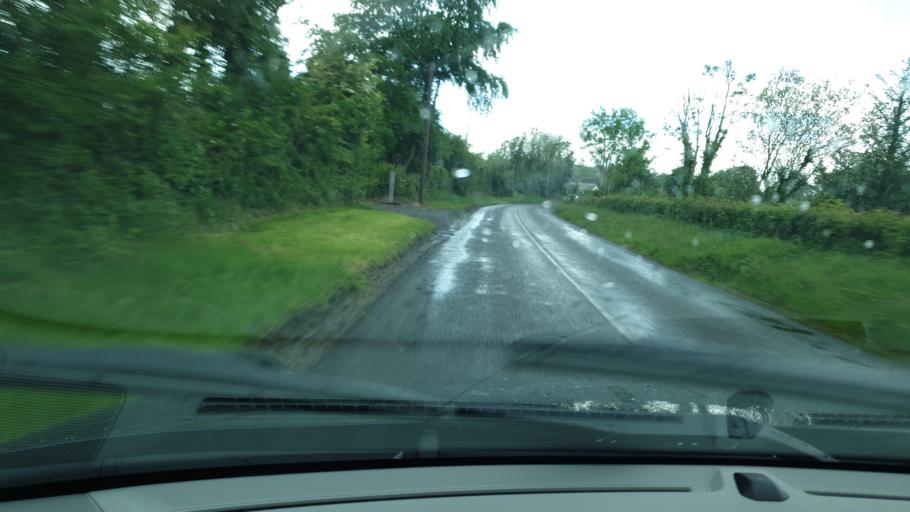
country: IE
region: Leinster
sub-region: Laois
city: Mountrath
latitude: 53.0578
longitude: -7.4127
